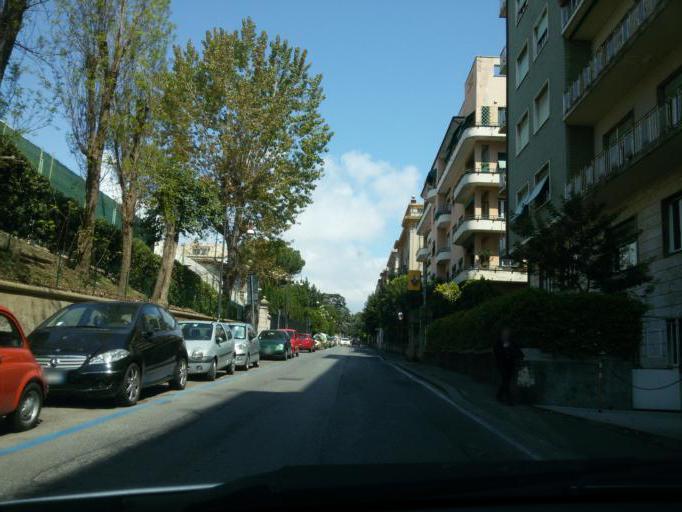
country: IT
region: Liguria
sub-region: Provincia di Genova
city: San Teodoro
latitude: 44.3944
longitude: 8.9580
